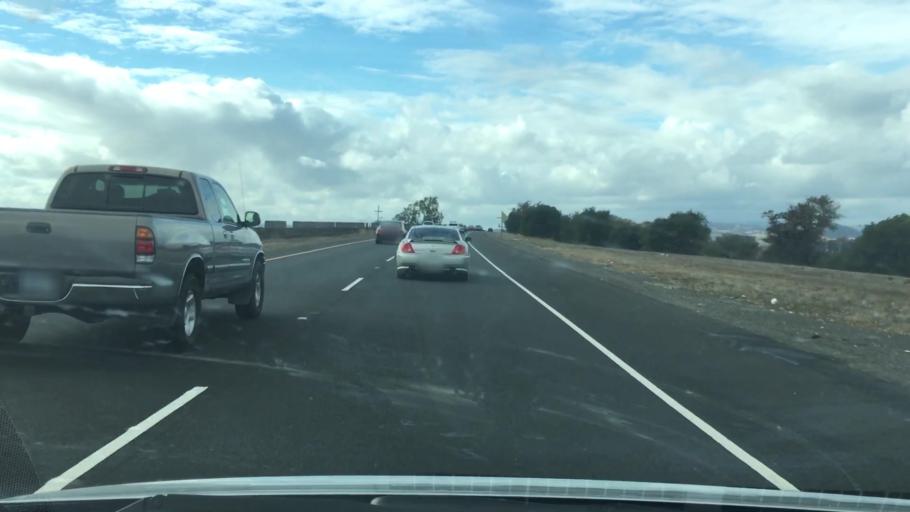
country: US
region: California
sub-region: Napa County
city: Napa
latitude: 38.2434
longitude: -122.2788
